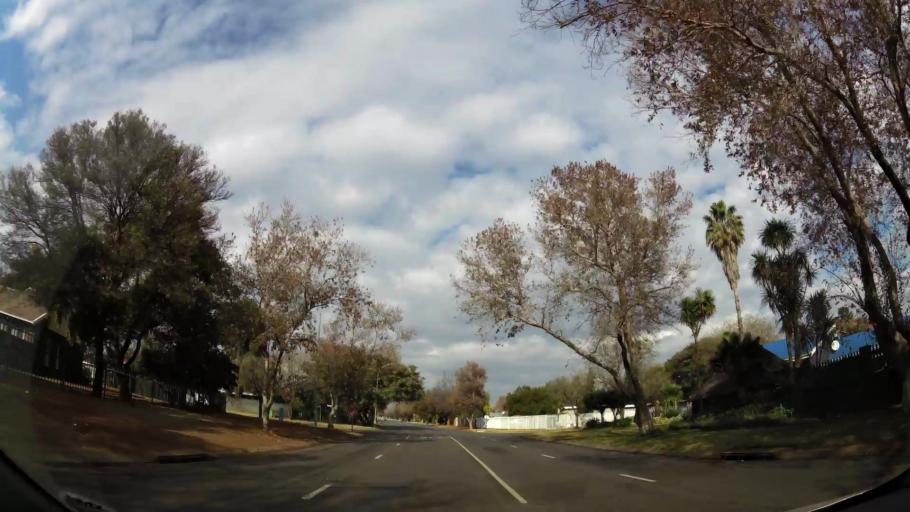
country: ZA
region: Gauteng
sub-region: Sedibeng District Municipality
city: Meyerton
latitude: -26.5521
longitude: 28.0328
